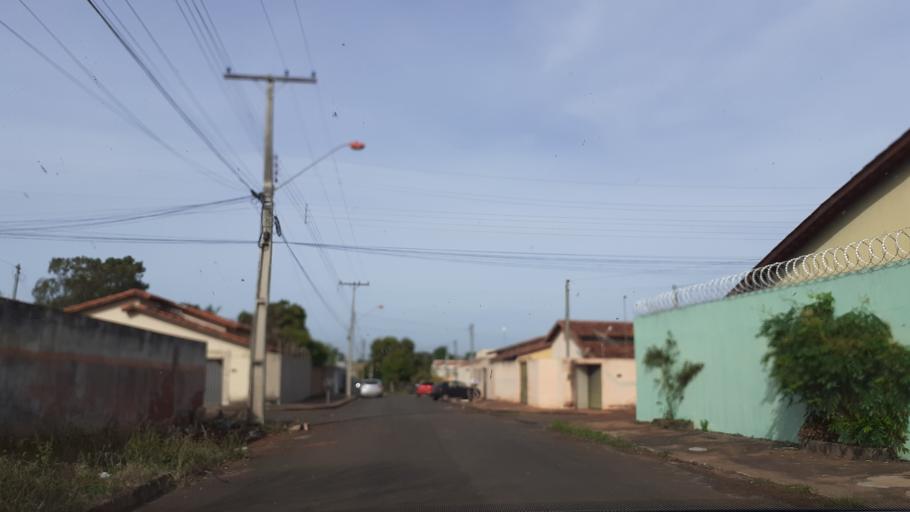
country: BR
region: Goias
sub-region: Itumbiara
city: Itumbiara
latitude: -18.4231
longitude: -49.2485
